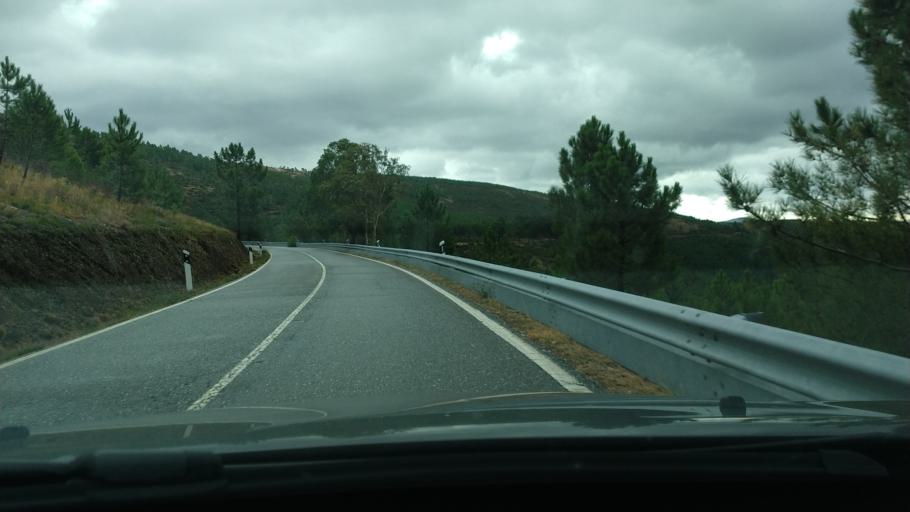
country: PT
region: Guarda
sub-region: Seia
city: Seia
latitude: 40.2483
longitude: -7.6781
